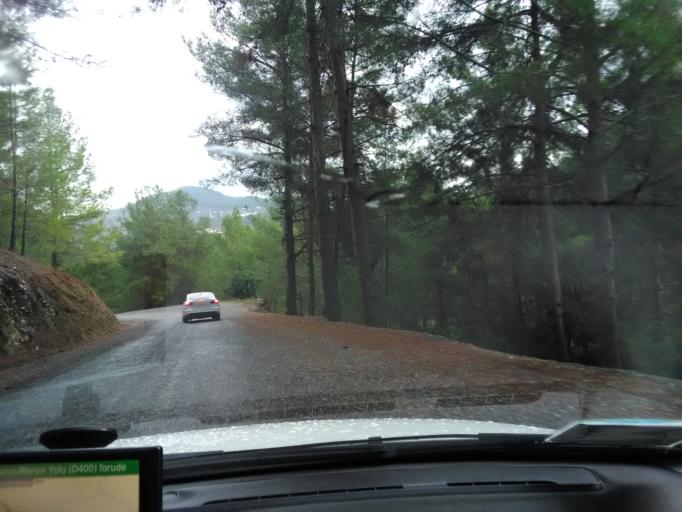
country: TR
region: Antalya
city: Gazipasa
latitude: 36.1645
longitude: 32.4352
